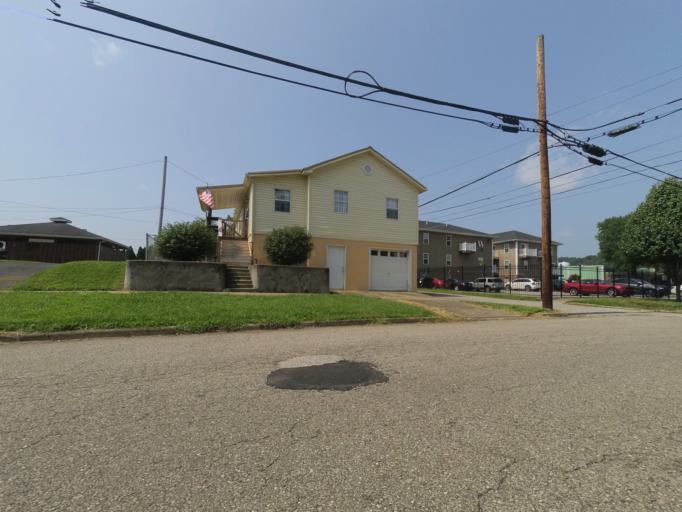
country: US
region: West Virginia
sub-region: Cabell County
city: Huntington
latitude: 38.4291
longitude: -82.4135
